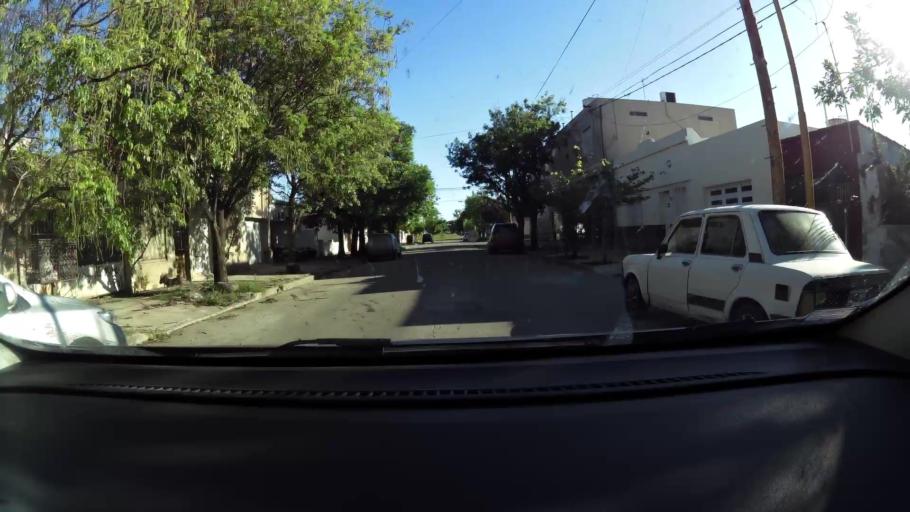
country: AR
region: Cordoba
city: San Francisco
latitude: -31.4372
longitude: -62.0911
